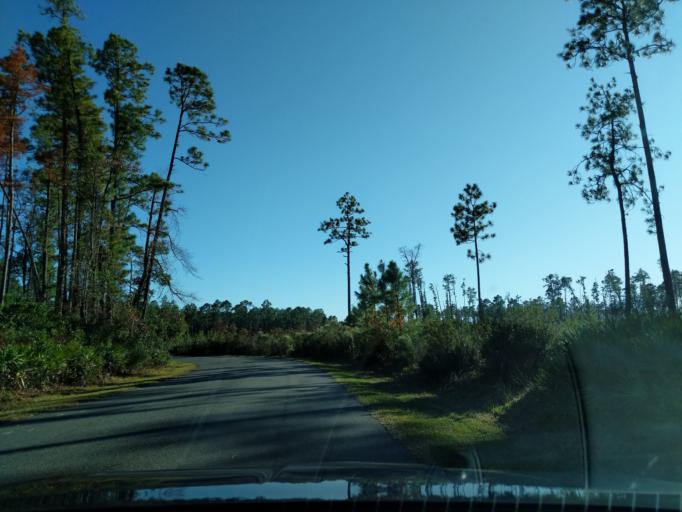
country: US
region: Georgia
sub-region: Charlton County
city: Folkston
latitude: 30.7231
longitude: -82.1400
